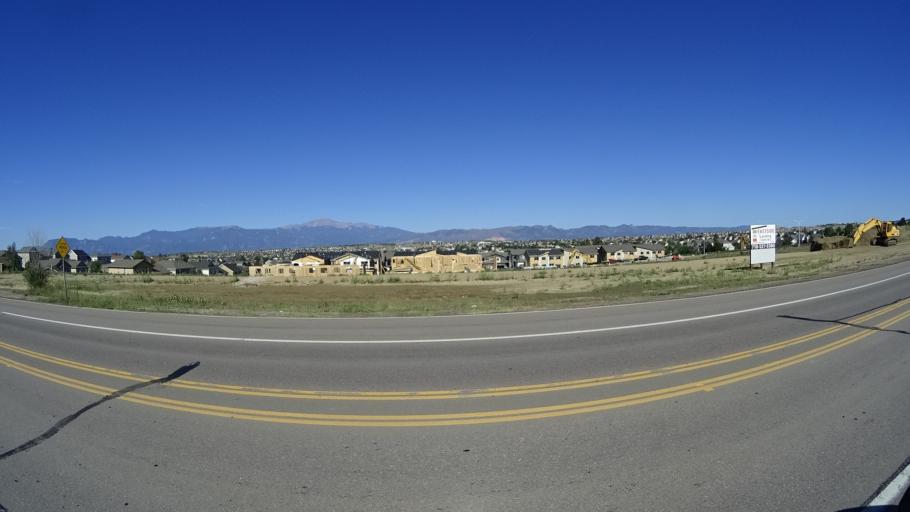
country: US
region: Colorado
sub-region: El Paso County
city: Cimarron Hills
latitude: 38.9109
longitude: -104.6827
